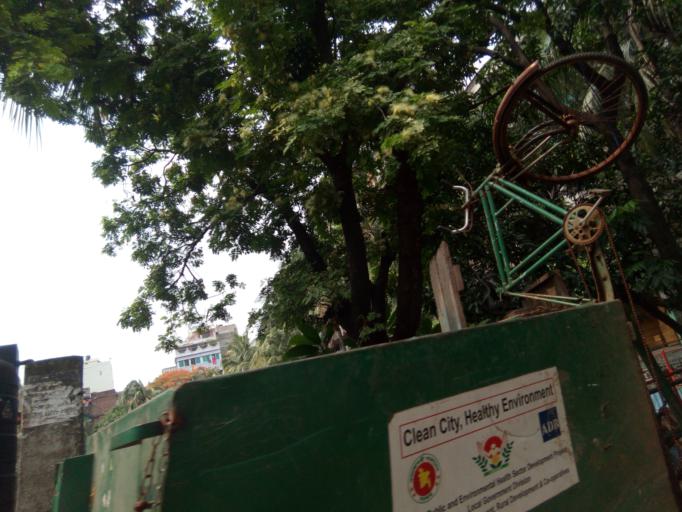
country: BD
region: Dhaka
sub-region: Dhaka
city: Dhaka
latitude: 23.7152
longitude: 90.4075
